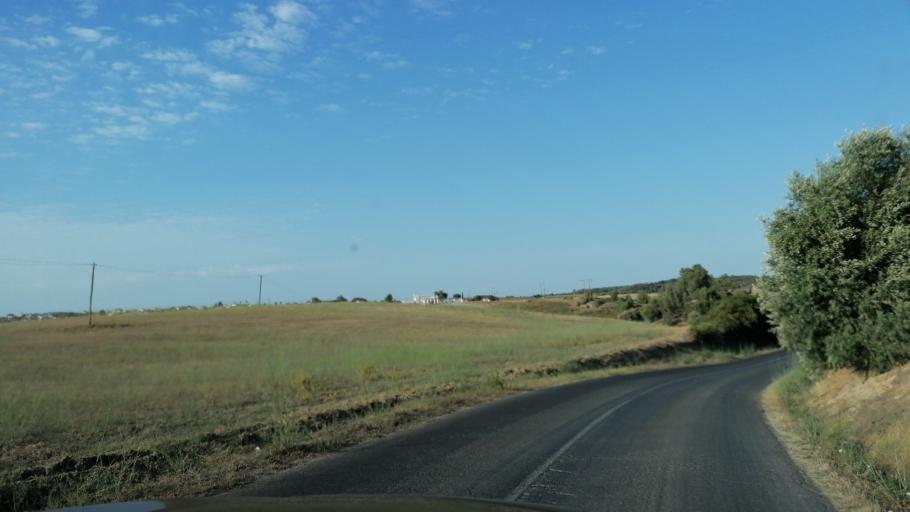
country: PT
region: Santarem
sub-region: Santarem
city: Santarem
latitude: 39.2795
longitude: -8.6582
